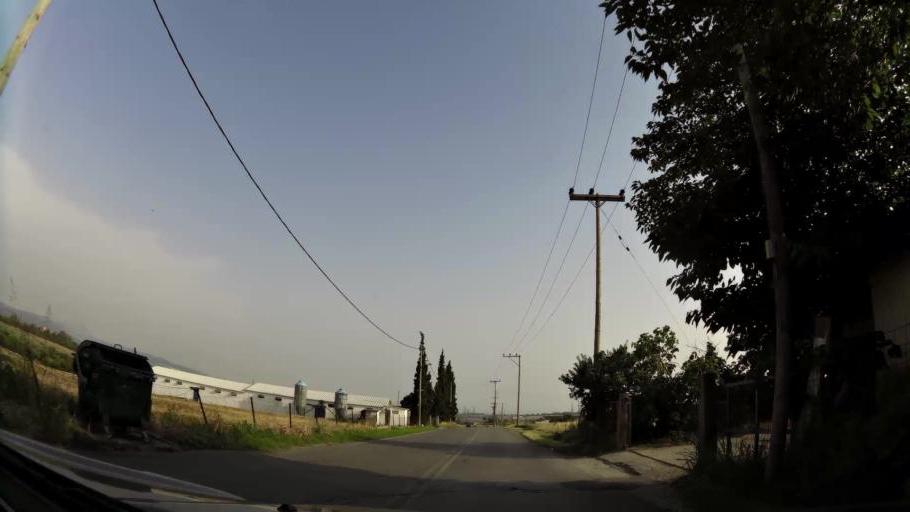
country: GR
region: Central Macedonia
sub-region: Nomos Thessalonikis
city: Oraiokastro
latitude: 40.7153
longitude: 22.9102
